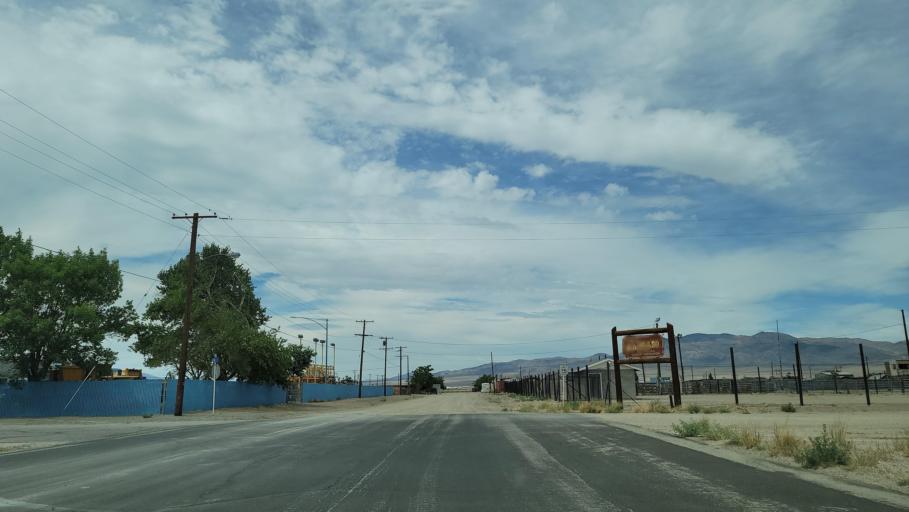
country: US
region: Nevada
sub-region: Mineral County
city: Hawthorne
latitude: 38.5290
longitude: -118.6161
